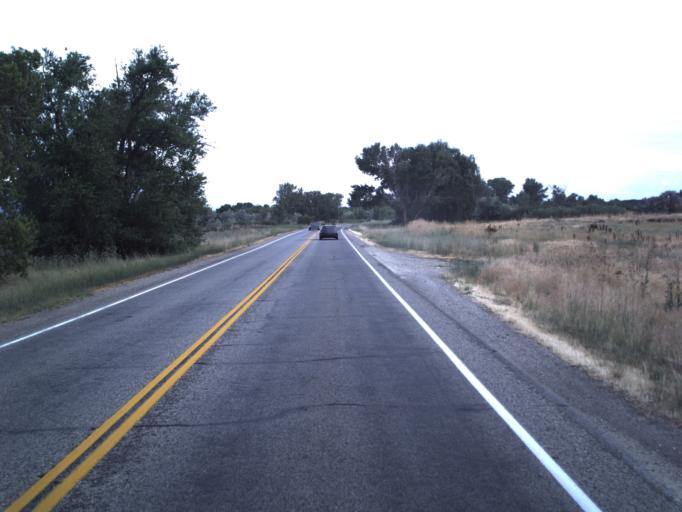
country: US
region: Utah
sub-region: Weber County
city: Marriott-Slaterville
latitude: 41.2618
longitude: -112.0260
